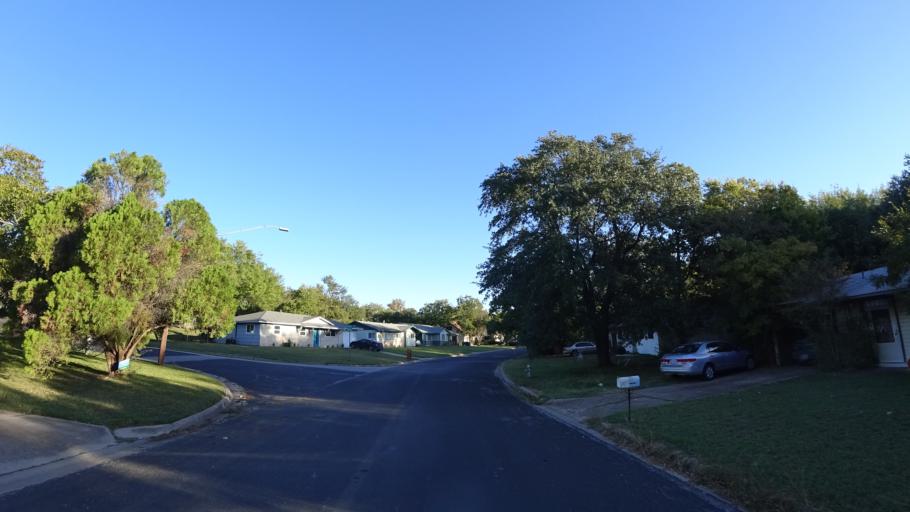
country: US
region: Texas
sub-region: Travis County
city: Austin
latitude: 30.3018
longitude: -97.6812
